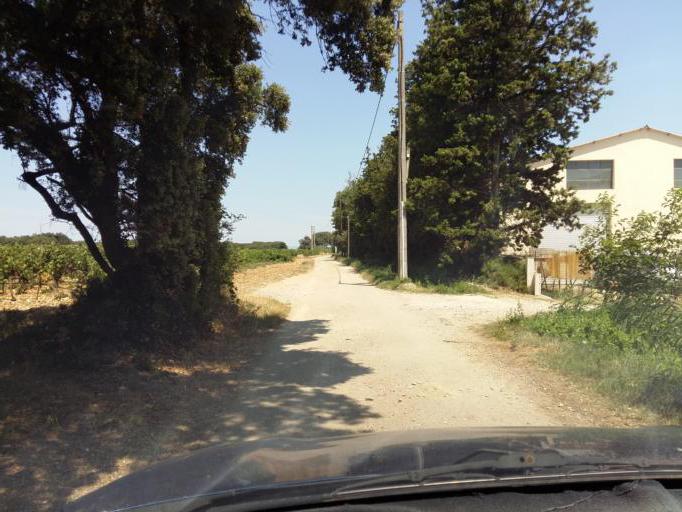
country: FR
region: Provence-Alpes-Cote d'Azur
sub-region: Departement du Vaucluse
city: Camaret-sur-Aigues
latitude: 44.1834
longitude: 4.8798
